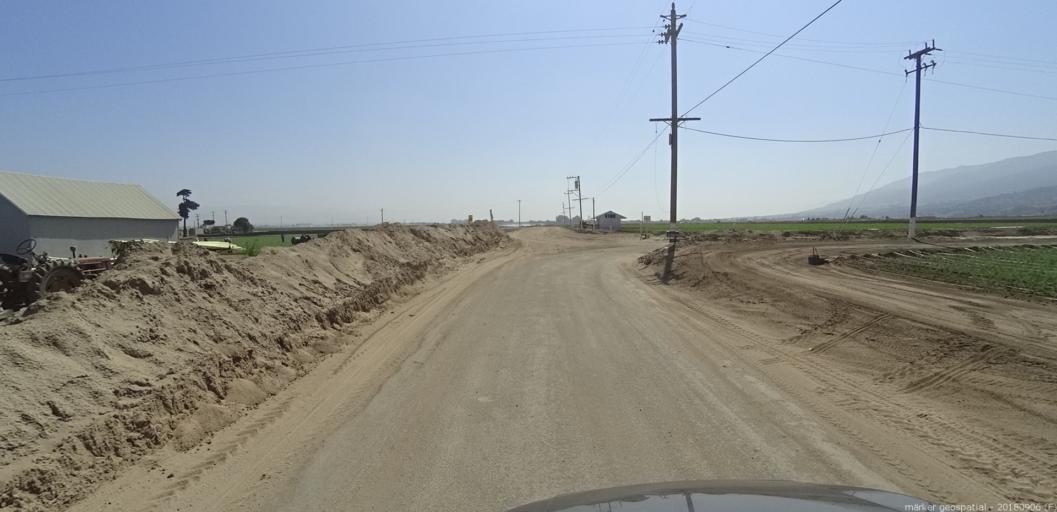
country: US
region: California
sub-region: Monterey County
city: Chualar
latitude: 36.5958
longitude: -121.6019
